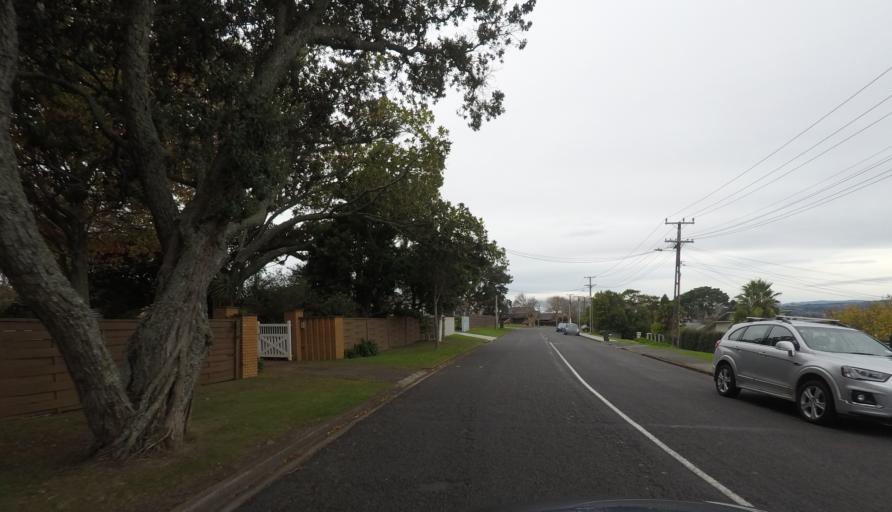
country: NZ
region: Auckland
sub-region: Auckland
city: Pakuranga
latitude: -36.8962
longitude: 174.9456
